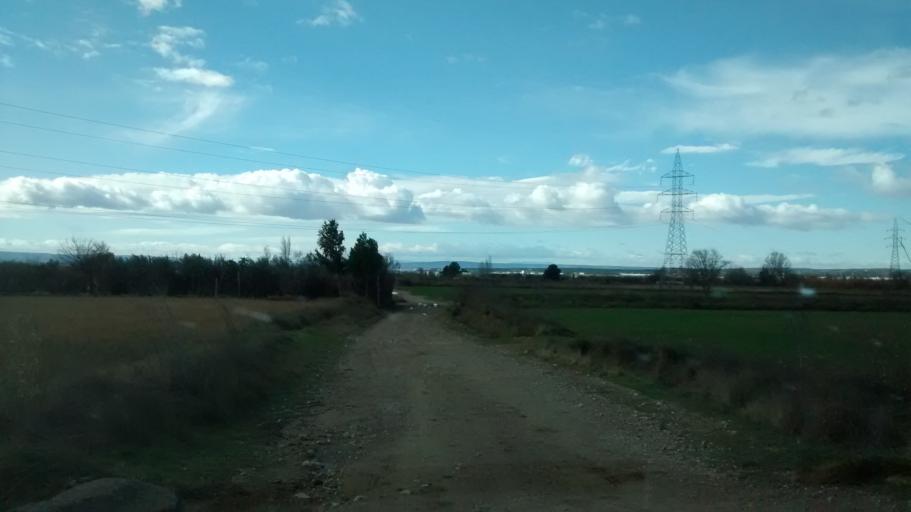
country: ES
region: Aragon
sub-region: Provincia de Zaragoza
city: Villanueva de Gallego
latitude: 41.7562
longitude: -0.7887
